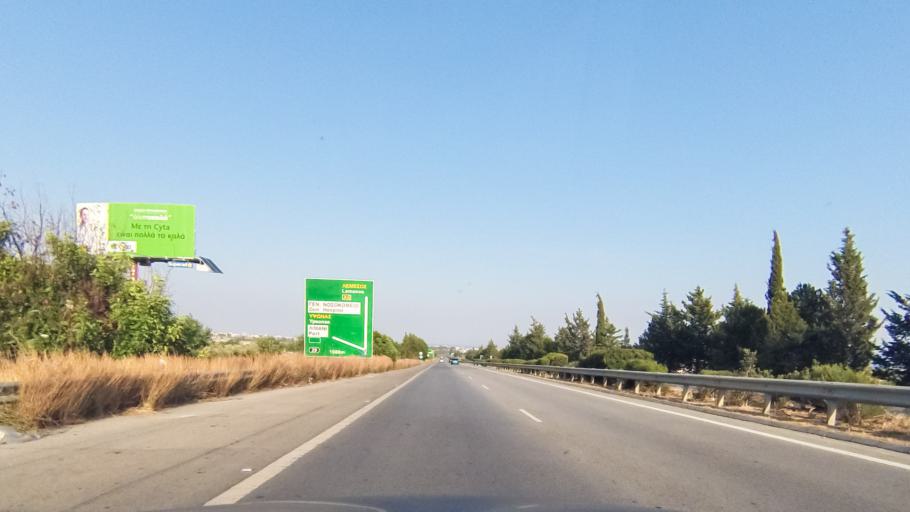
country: CY
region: Limassol
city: Ypsonas
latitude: 34.6932
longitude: 32.9724
